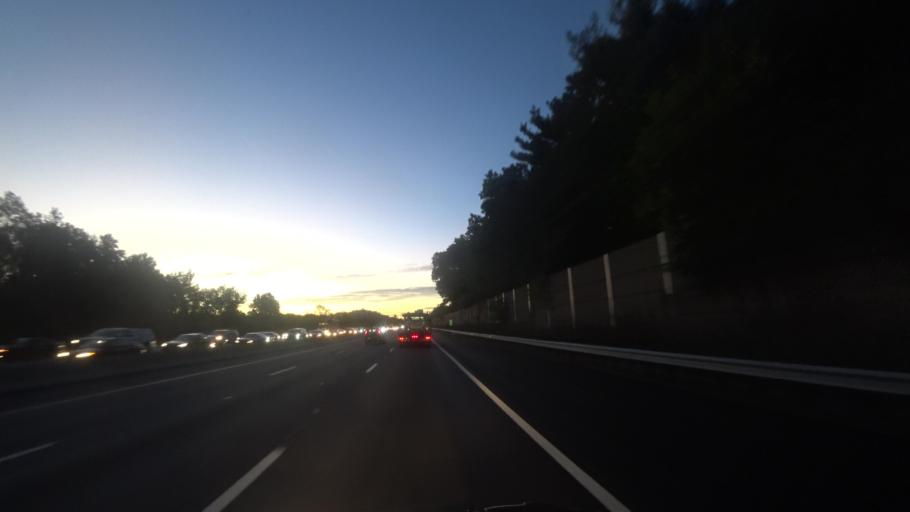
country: US
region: Massachusetts
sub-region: Essex County
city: Lynnfield
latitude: 42.5213
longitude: -71.0562
